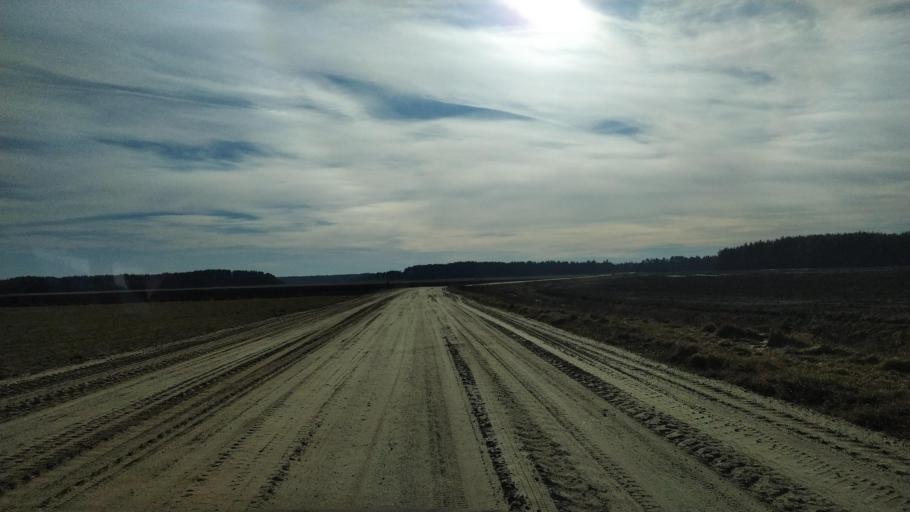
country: BY
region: Brest
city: Pruzhany
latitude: 52.5676
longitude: 24.2961
